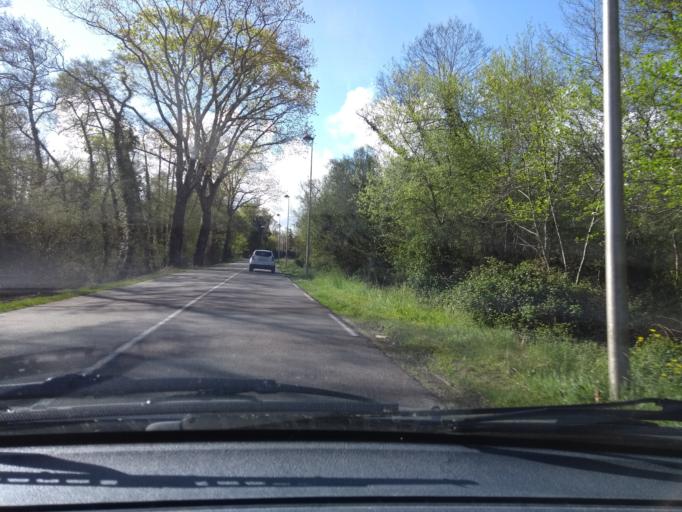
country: FR
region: Aquitaine
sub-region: Departement des Landes
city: Parentis-en-Born
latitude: 44.3427
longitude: -1.0815
